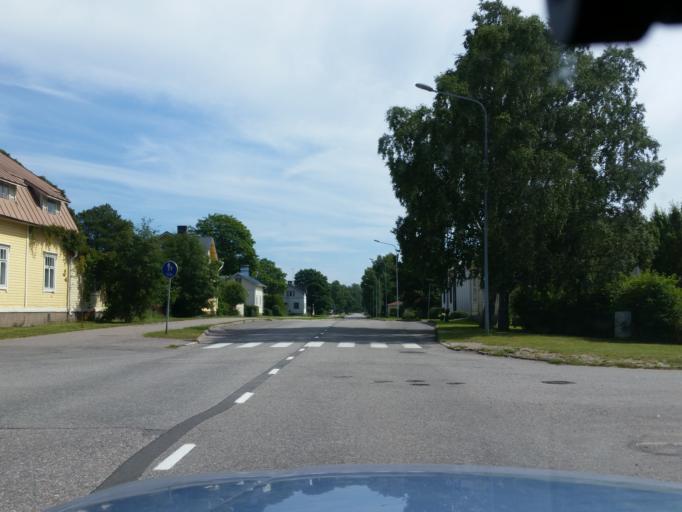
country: FI
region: Uusimaa
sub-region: Raaseporin
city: Hanko
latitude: 59.8339
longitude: 22.9506
